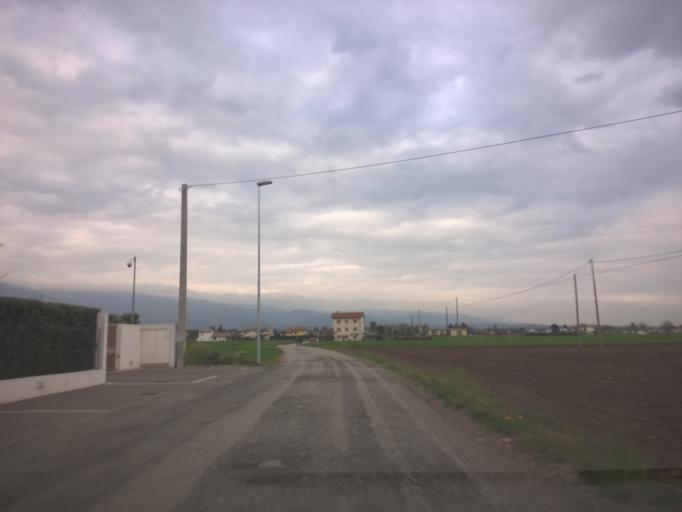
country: IT
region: Veneto
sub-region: Provincia di Vicenza
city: Thiene
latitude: 45.6926
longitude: 11.4699
